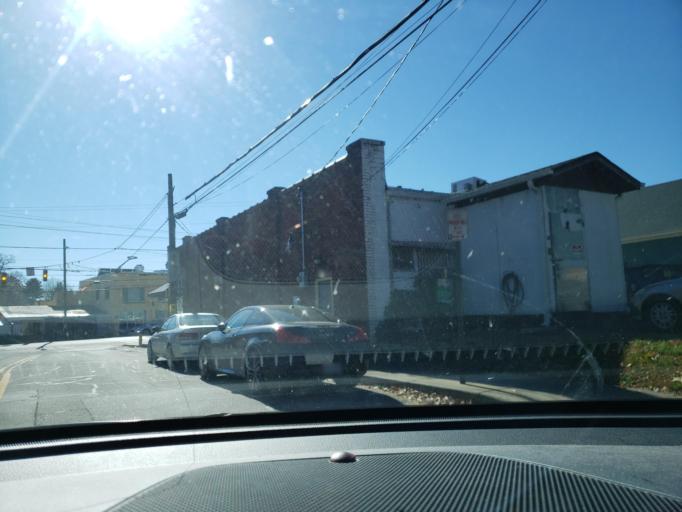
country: US
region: North Carolina
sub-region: Buncombe County
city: Asheville
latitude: 35.5792
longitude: -82.5888
